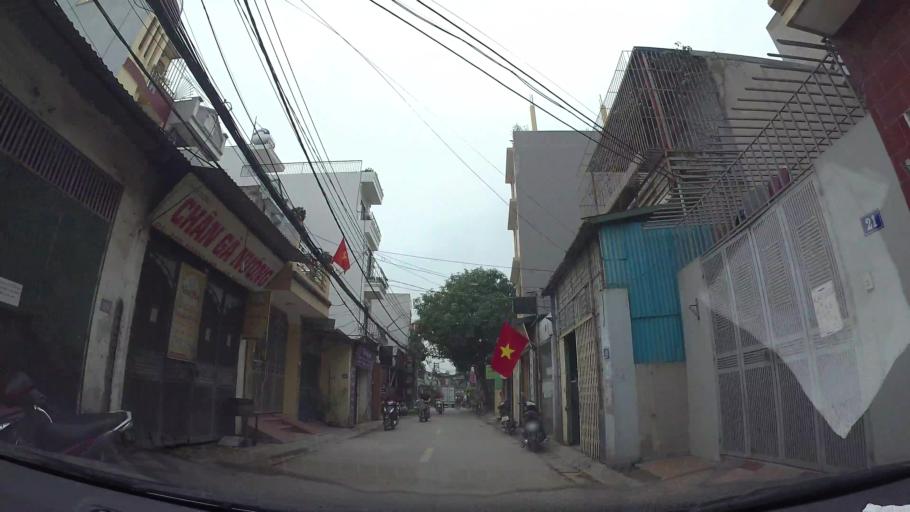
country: VN
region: Ha Noi
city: Hai BaTrung
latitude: 20.9923
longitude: 105.8887
